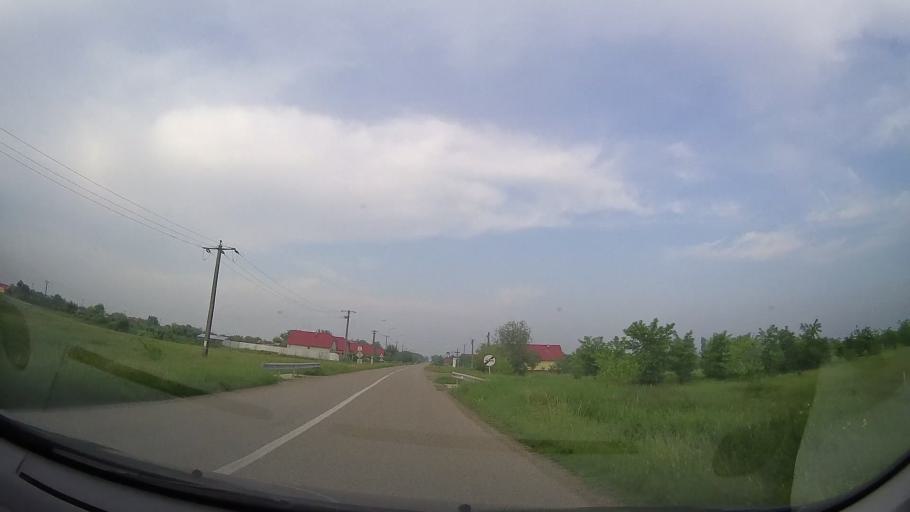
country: RO
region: Timis
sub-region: Comuna Foeni
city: Foeni
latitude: 45.5048
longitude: 20.8794
